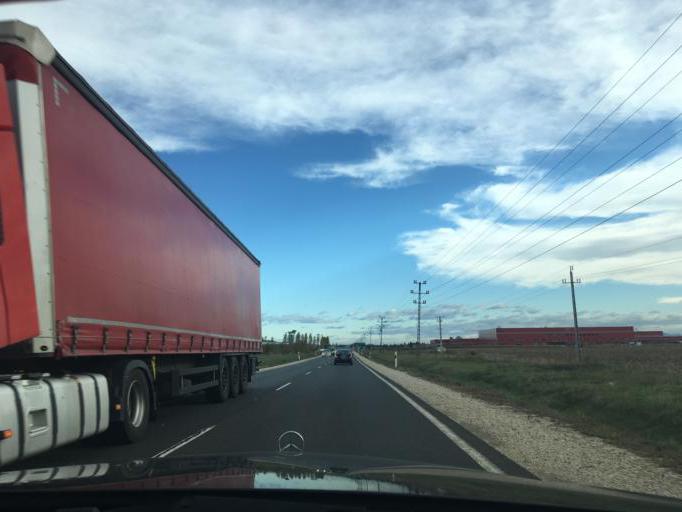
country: HU
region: Borsod-Abauj-Zemplen
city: Szikszo
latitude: 48.1718
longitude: 20.9120
